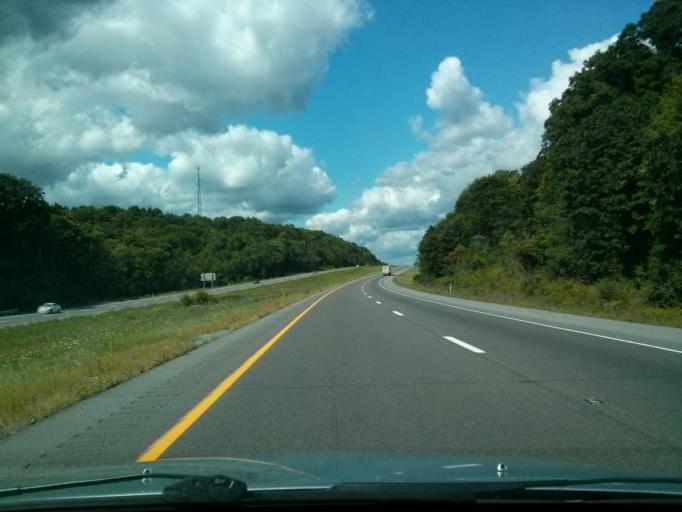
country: US
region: Pennsylvania
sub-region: Clearfield County
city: Treasure Lake
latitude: 41.1204
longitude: -78.6299
